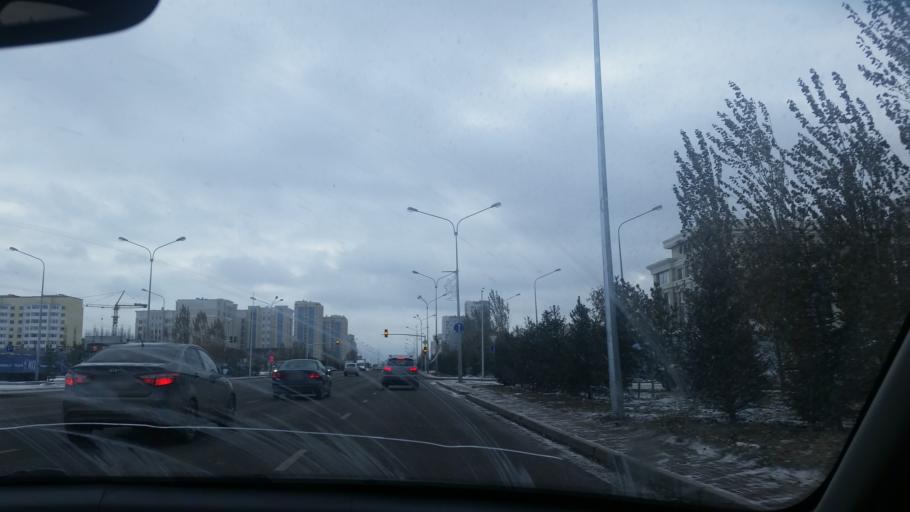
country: KZ
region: Astana Qalasy
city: Astana
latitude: 51.1012
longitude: 71.4289
